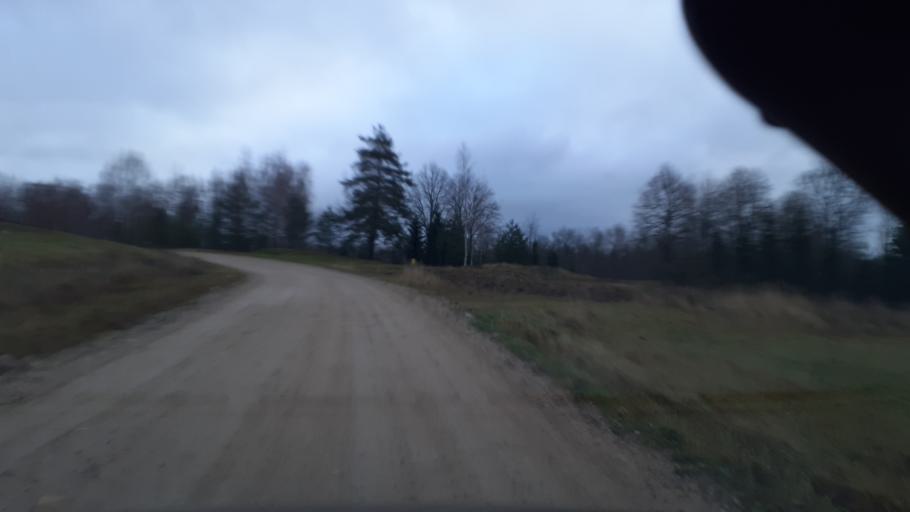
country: LV
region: Alsunga
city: Alsunga
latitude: 56.8793
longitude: 21.6941
